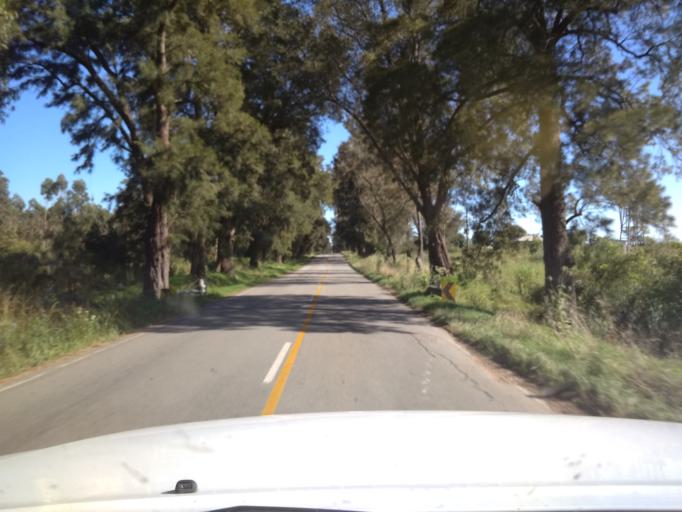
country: UY
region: Canelones
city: San Bautista
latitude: -34.3729
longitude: -55.9595
